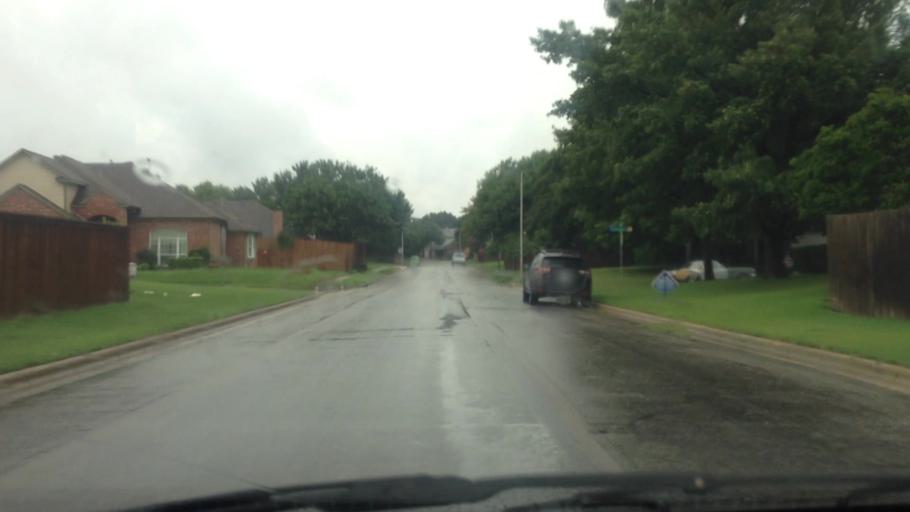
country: US
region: Texas
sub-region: Tarrant County
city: Watauga
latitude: 32.8867
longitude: -97.2318
